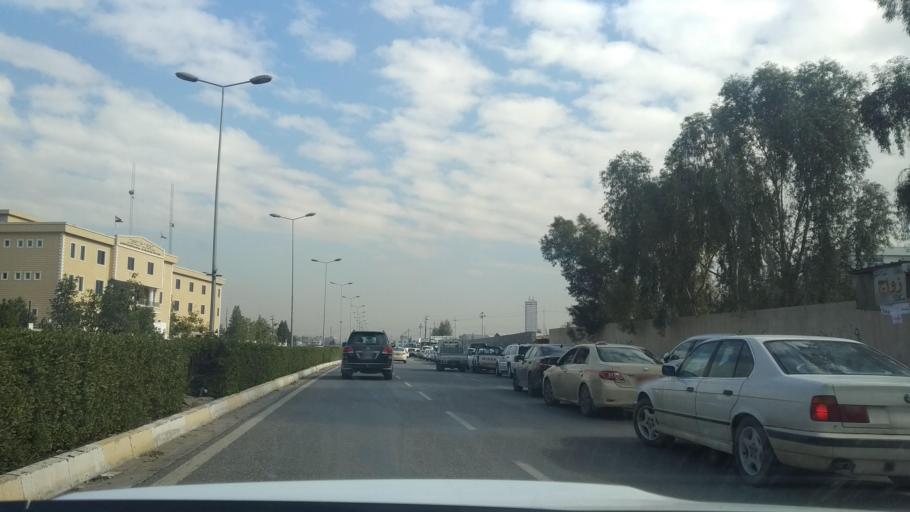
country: IQ
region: Arbil
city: Erbil
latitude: 36.1818
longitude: 43.9806
